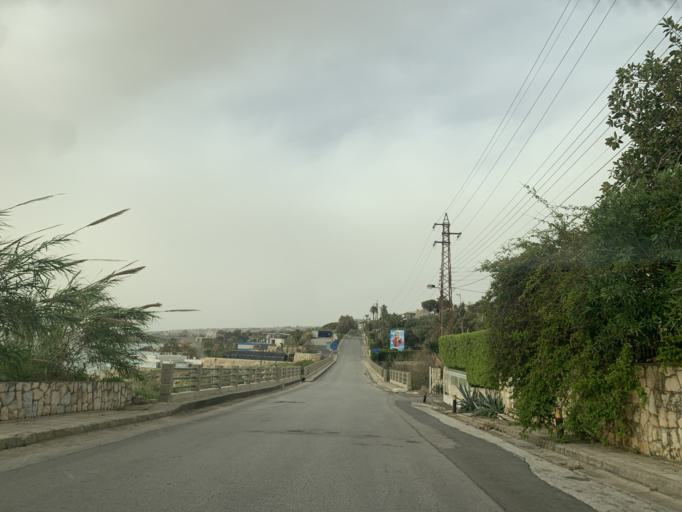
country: LB
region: Mont-Liban
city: Jbail
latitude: 34.1014
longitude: 35.6515
